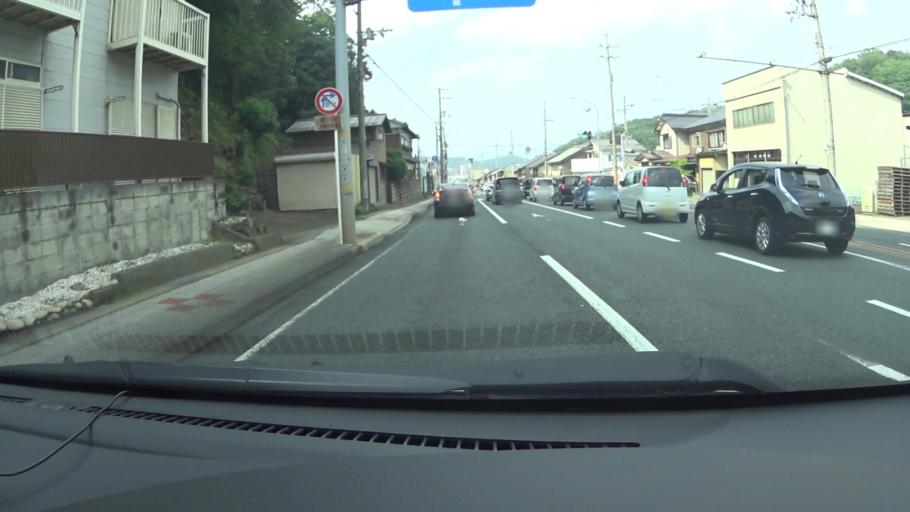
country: JP
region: Kyoto
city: Maizuru
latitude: 35.4668
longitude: 135.3640
